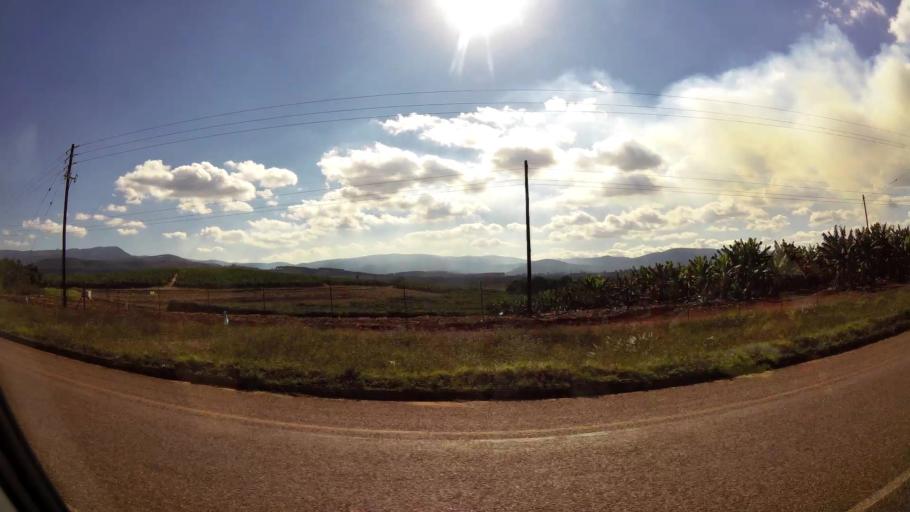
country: ZA
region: Limpopo
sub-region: Mopani District Municipality
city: Tzaneen
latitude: -23.8042
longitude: 30.1142
